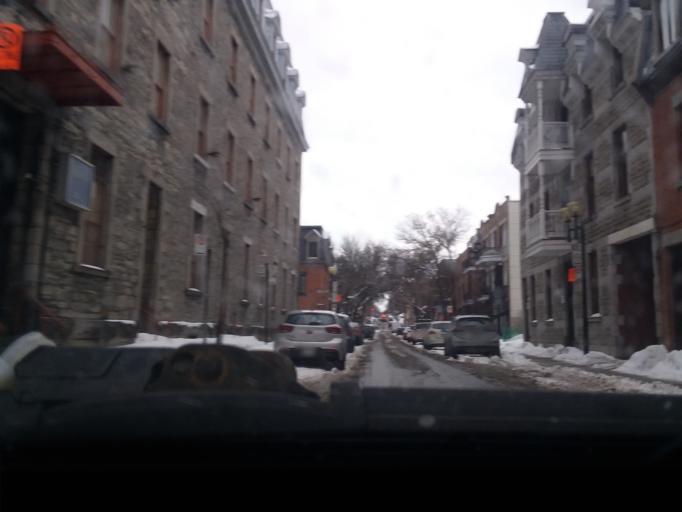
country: CA
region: Quebec
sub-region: Montreal
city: Montreal
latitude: 45.5192
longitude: -73.5532
